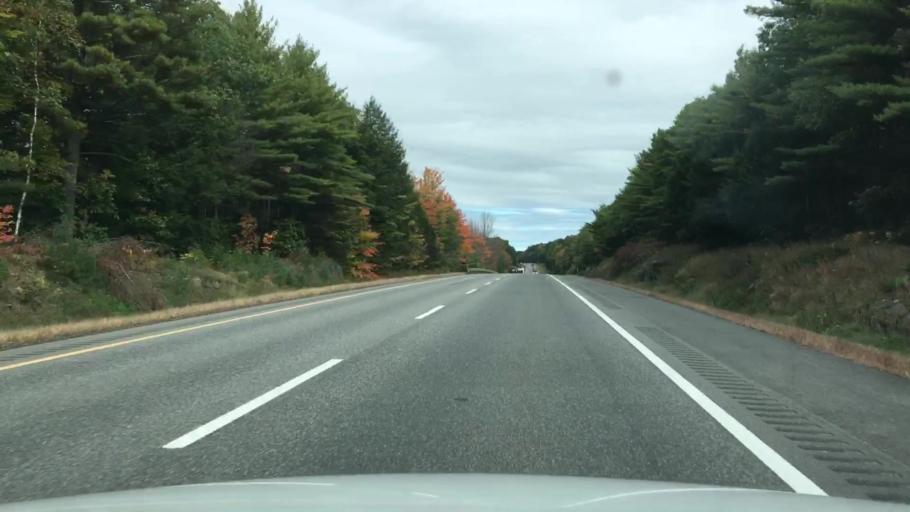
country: US
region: Maine
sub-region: Kennebec County
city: Sidney
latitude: 44.3883
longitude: -69.7606
